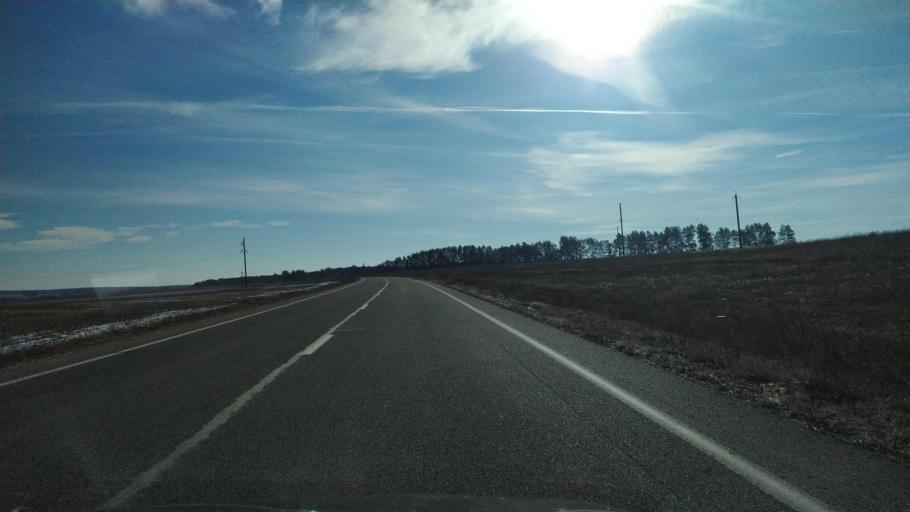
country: BY
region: Brest
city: Kamyanyets
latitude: 52.4072
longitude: 23.8582
